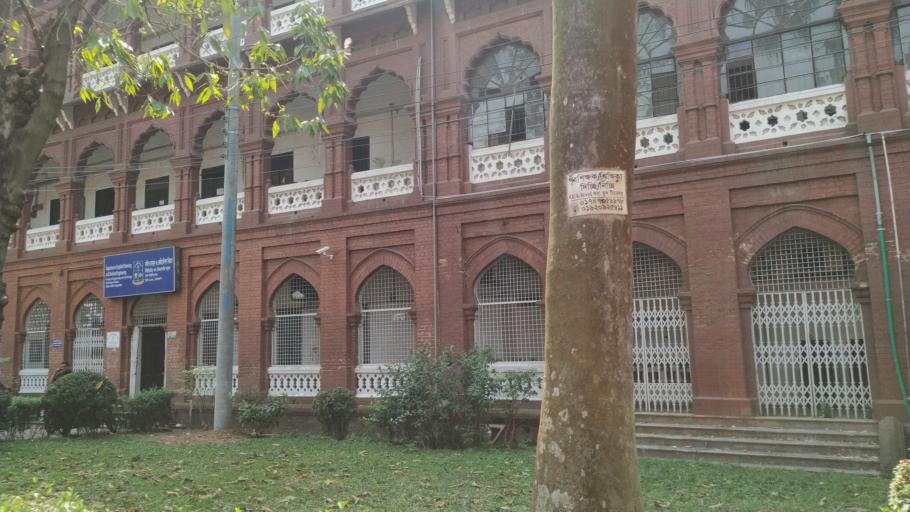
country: BD
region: Dhaka
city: Paltan
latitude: 23.7272
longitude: 90.4023
